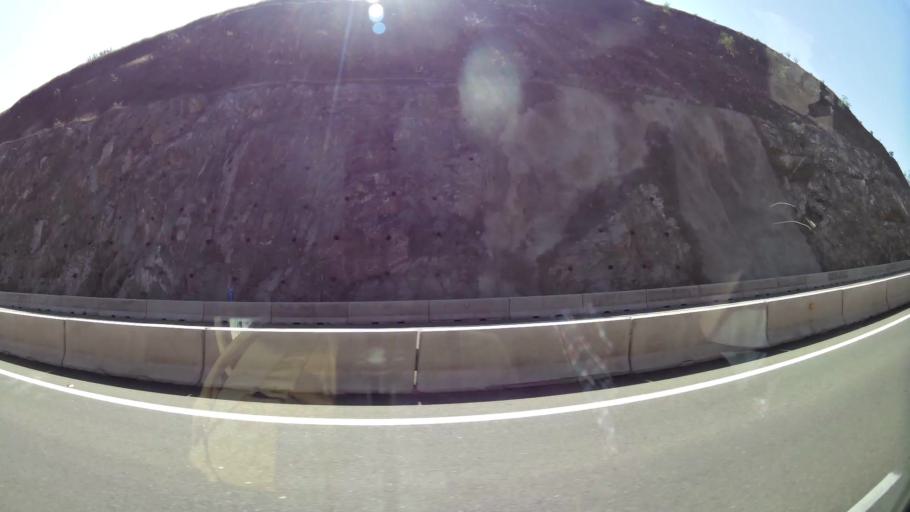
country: CL
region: Santiago Metropolitan
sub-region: Provincia de Chacabuco
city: Chicureo Abajo
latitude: -33.3108
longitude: -70.6523
